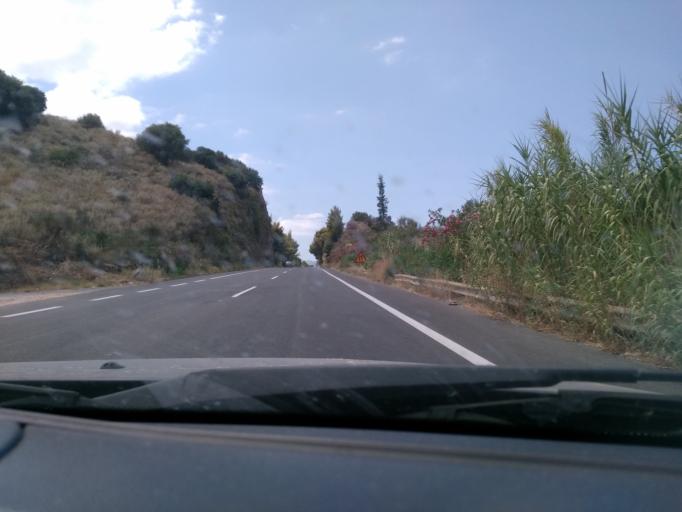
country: GR
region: Crete
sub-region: Nomos Chanias
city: Georgioupolis
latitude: 35.3626
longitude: 24.2436
